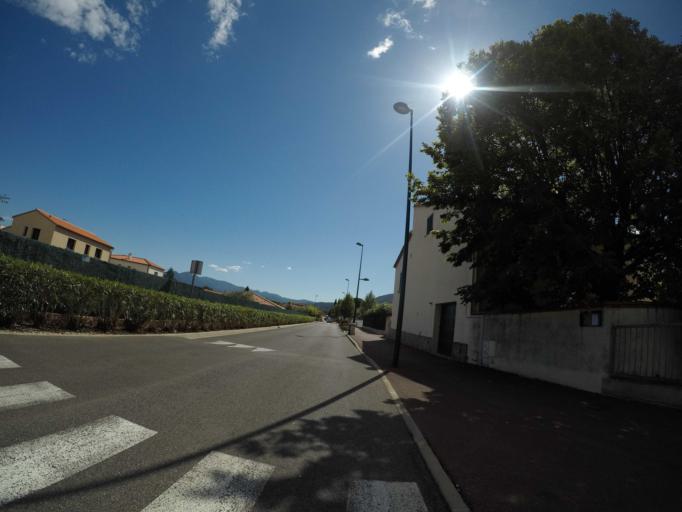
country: FR
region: Languedoc-Roussillon
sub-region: Departement des Pyrenees-Orientales
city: Ceret
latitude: 42.4926
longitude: 2.7369
